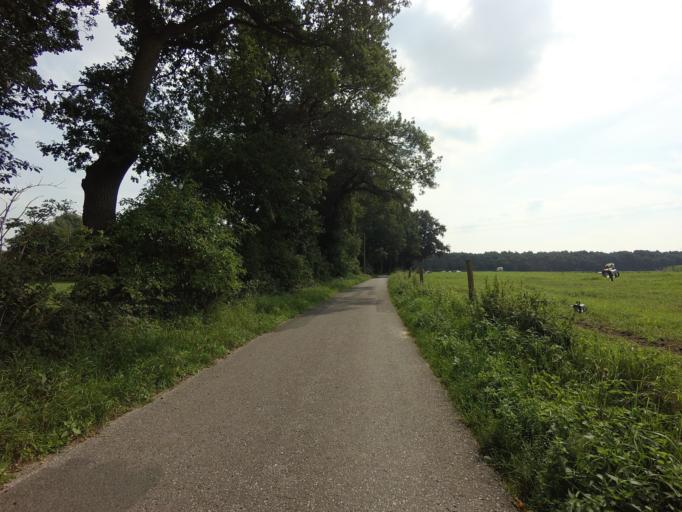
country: NL
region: Gelderland
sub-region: Gemeente Montferland
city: s-Heerenberg
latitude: 51.8880
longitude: 6.1722
